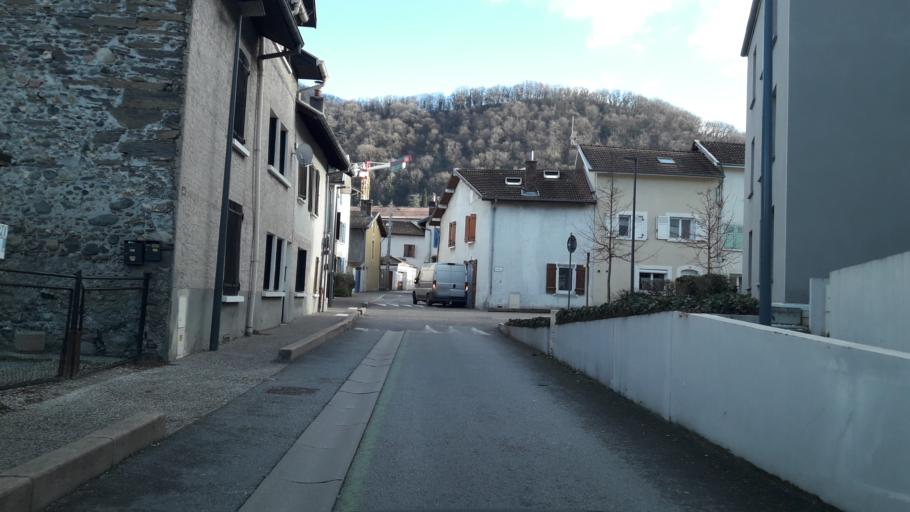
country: FR
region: Rhone-Alpes
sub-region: Departement de l'Isere
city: Gieres
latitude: 45.1838
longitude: 5.7908
